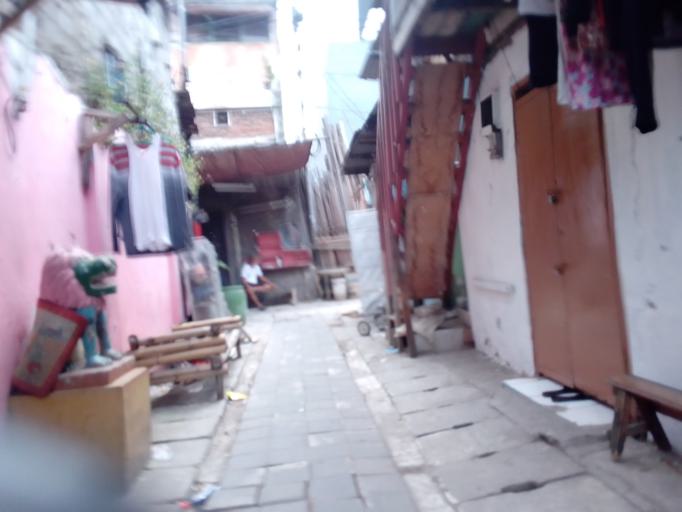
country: ID
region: Jakarta Raya
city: Jakarta
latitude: -6.2011
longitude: 106.8241
